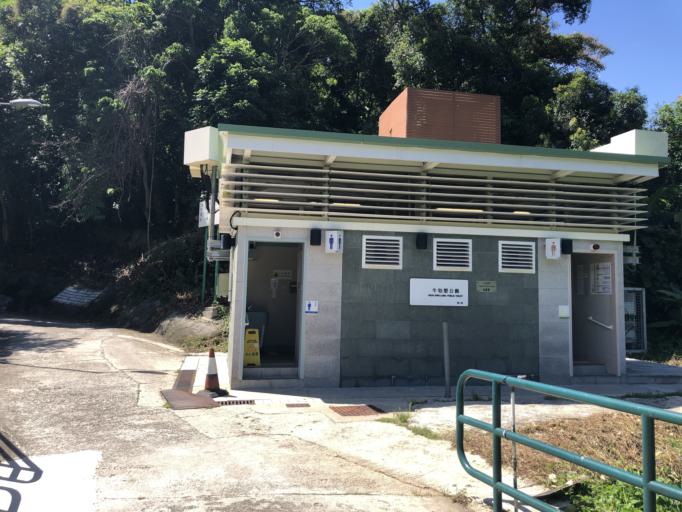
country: HK
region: Tuen Mun
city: Tuen Mun
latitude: 22.2918
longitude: 113.9776
